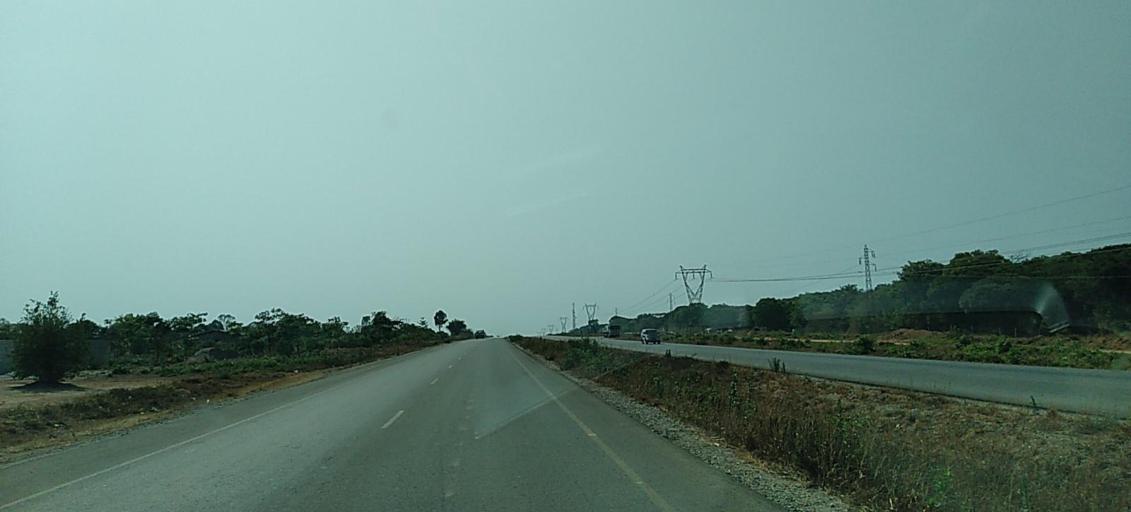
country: ZM
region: Copperbelt
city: Chingola
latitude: -12.5881
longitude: 27.9428
